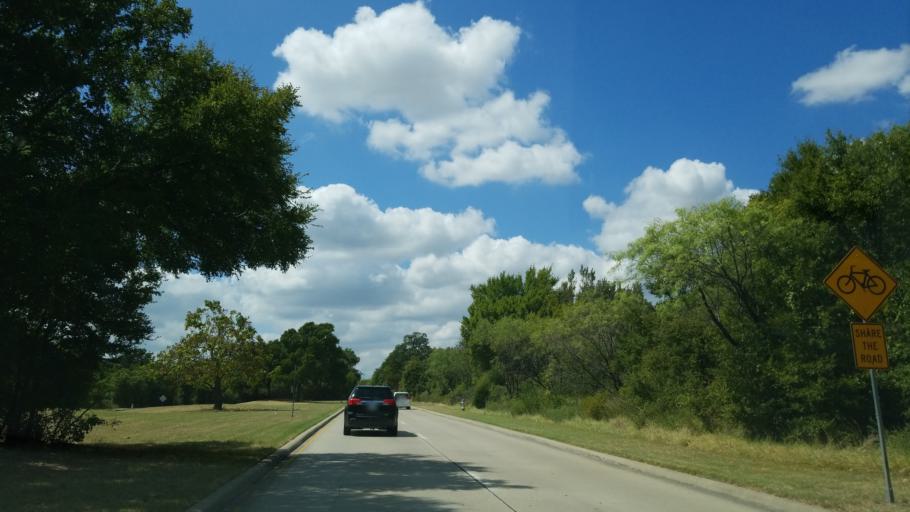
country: US
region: Texas
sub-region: Tarrant County
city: Grapevine
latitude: 32.9222
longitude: -97.0935
